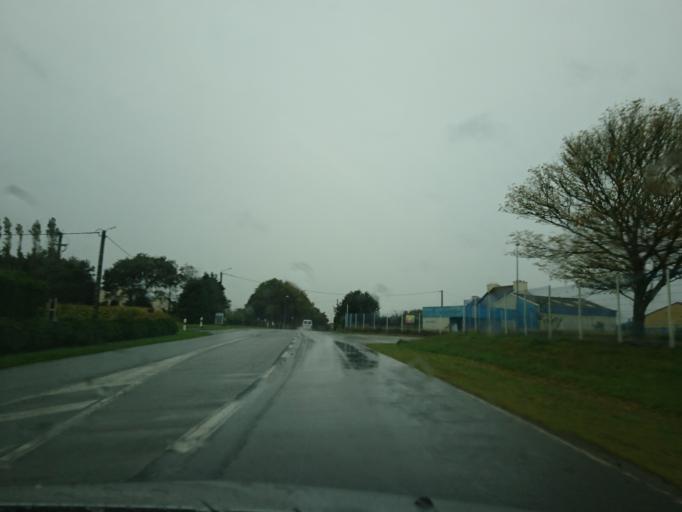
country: FR
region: Brittany
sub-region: Departement du Finistere
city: Le Drennec
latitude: 48.5281
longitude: -4.3782
